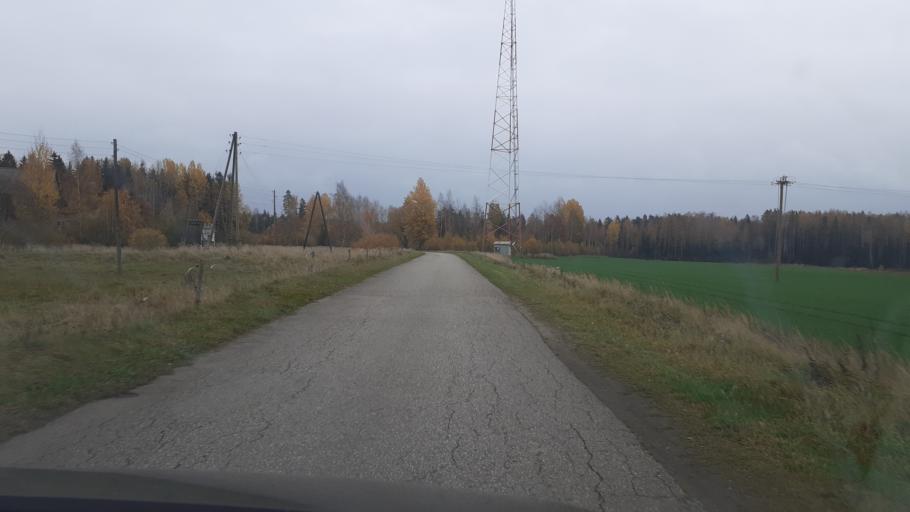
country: LV
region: Skrunda
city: Skrunda
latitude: 56.8562
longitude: 22.2378
